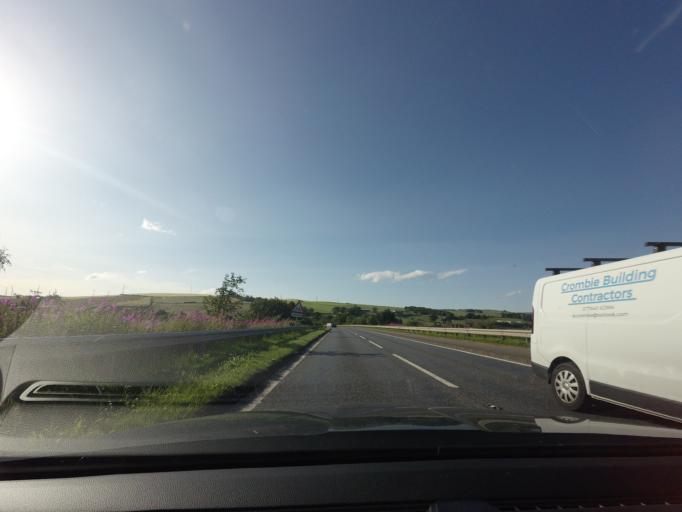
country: GB
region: Scotland
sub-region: Highland
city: Conon Bridge
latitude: 57.5765
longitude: -4.4334
